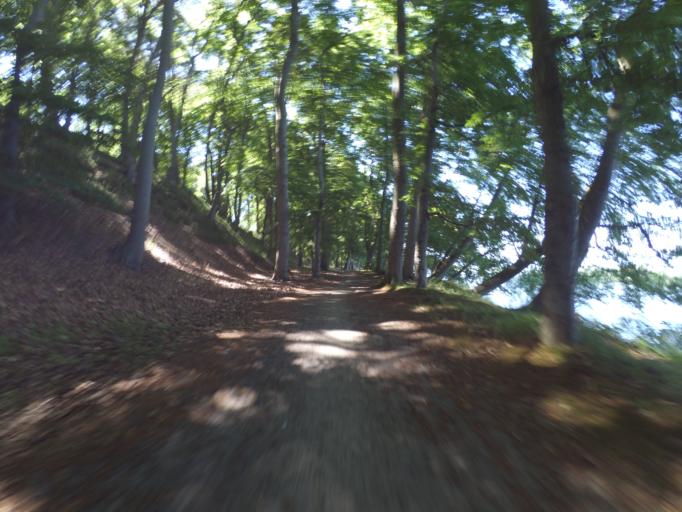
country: DE
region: Mecklenburg-Vorpommern
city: Malchow
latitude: 53.4734
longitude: 12.3495
